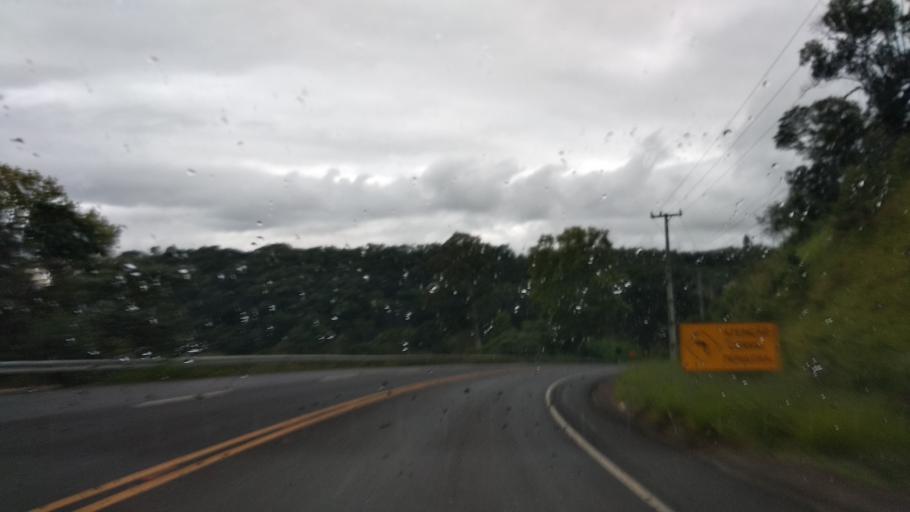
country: BR
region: Santa Catarina
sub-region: Videira
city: Videira
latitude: -27.0520
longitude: -51.1753
